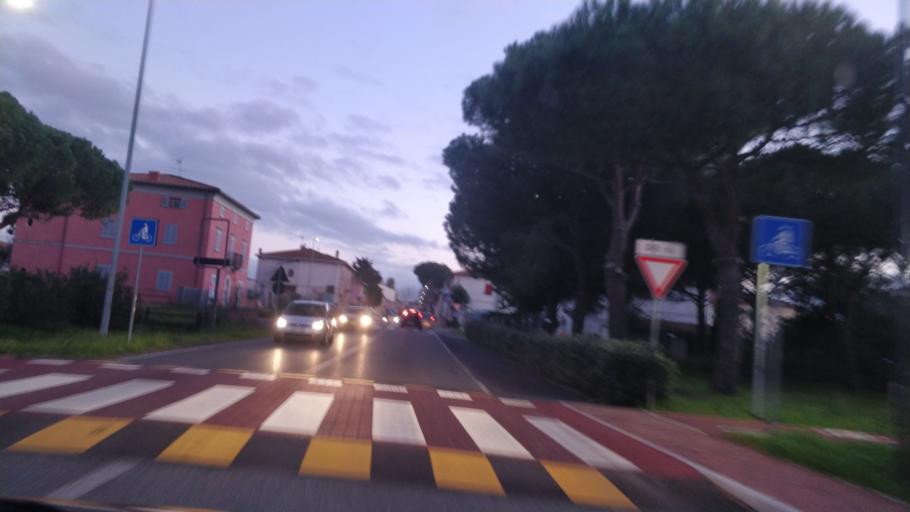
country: IT
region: Tuscany
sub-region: Provincia di Livorno
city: Vada
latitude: 43.3546
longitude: 10.4556
